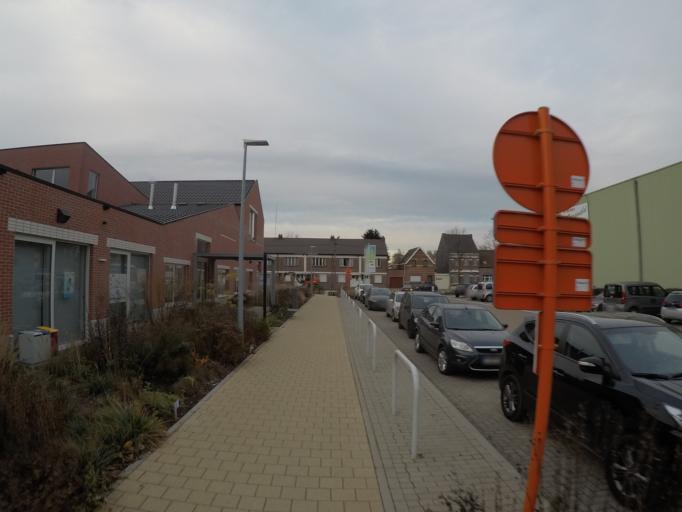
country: BE
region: Flanders
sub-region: Provincie Antwerpen
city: Berlaar
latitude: 51.1190
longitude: 4.6683
